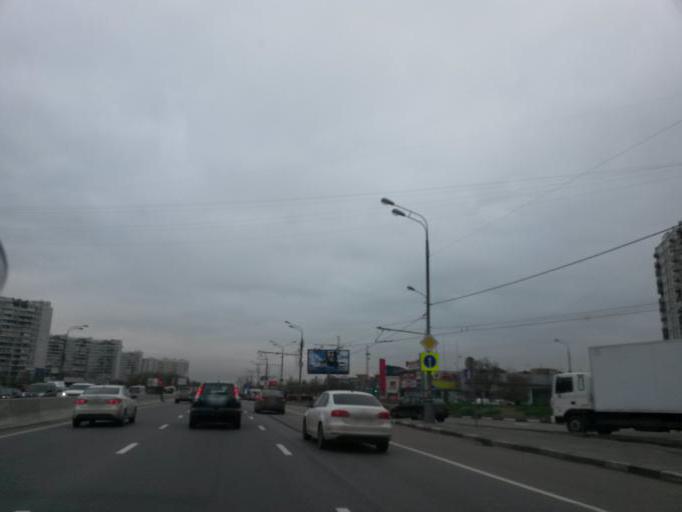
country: RU
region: Moscow
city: Annino
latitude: 55.5824
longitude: 37.5973
